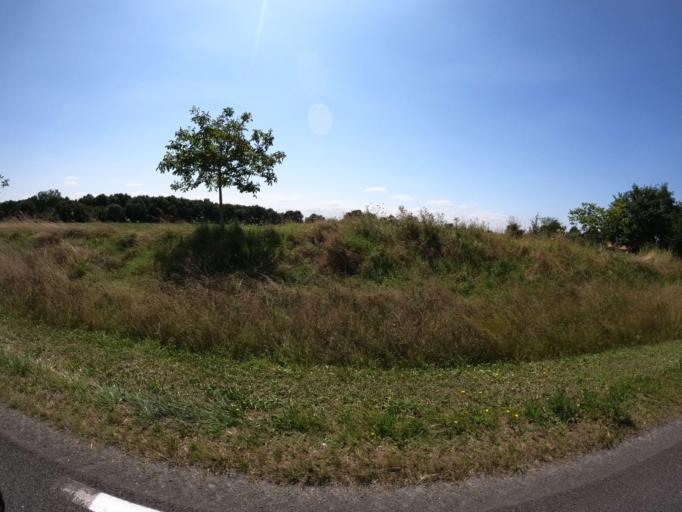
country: FR
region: Poitou-Charentes
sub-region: Departement de la Vienne
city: Charroux
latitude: 46.1520
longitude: 0.4016
